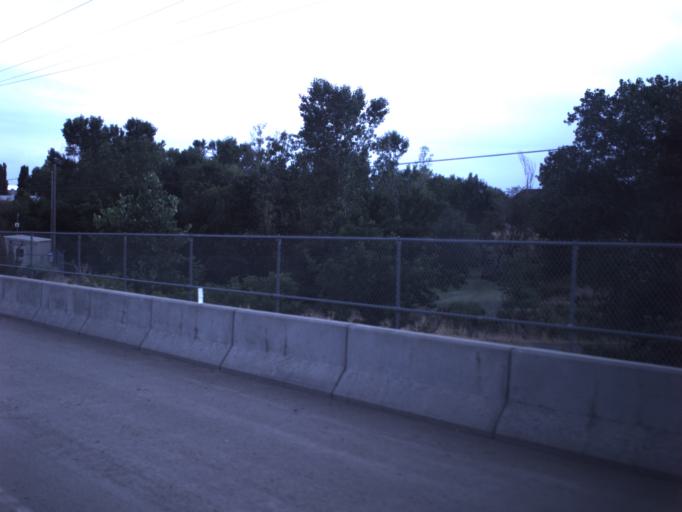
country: US
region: Utah
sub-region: Weber County
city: Marriott-Slaterville
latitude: 41.2415
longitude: -112.0255
